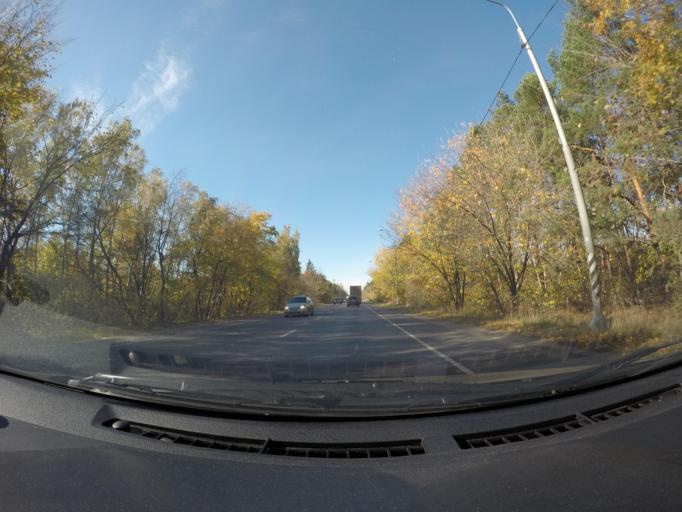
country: RU
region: Moskovskaya
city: Rodniki
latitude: 55.6560
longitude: 38.0785
